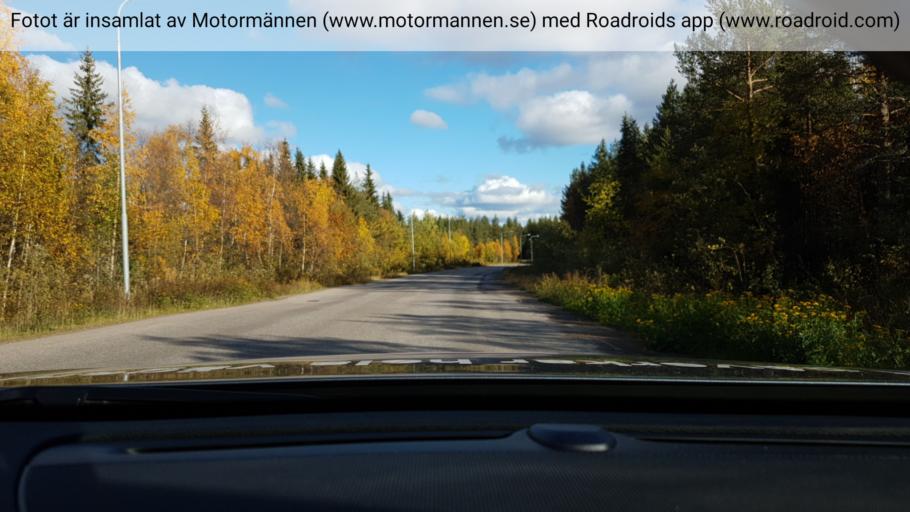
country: SE
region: Norrbotten
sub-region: Gallivare Kommun
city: Malmberget
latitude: 67.1660
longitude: 20.6513
